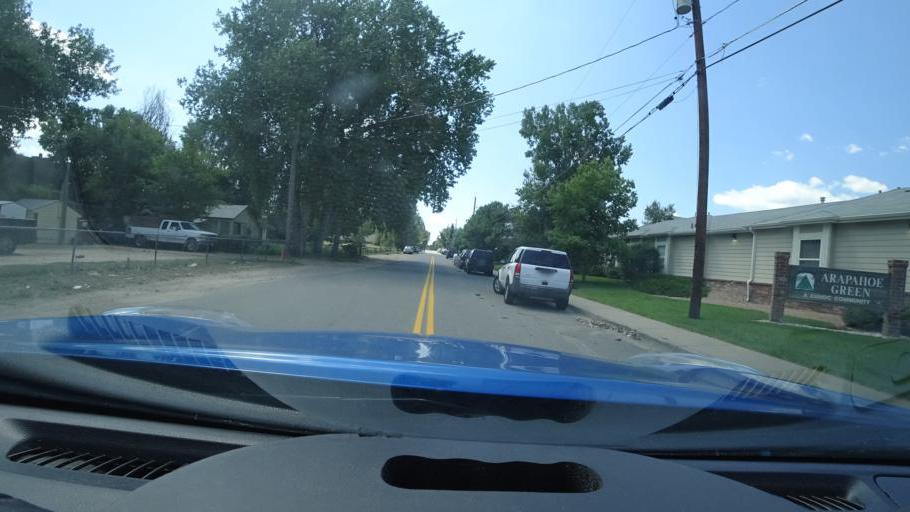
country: US
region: Colorado
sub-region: Arapahoe County
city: Glendale
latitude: 39.6960
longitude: -104.8859
